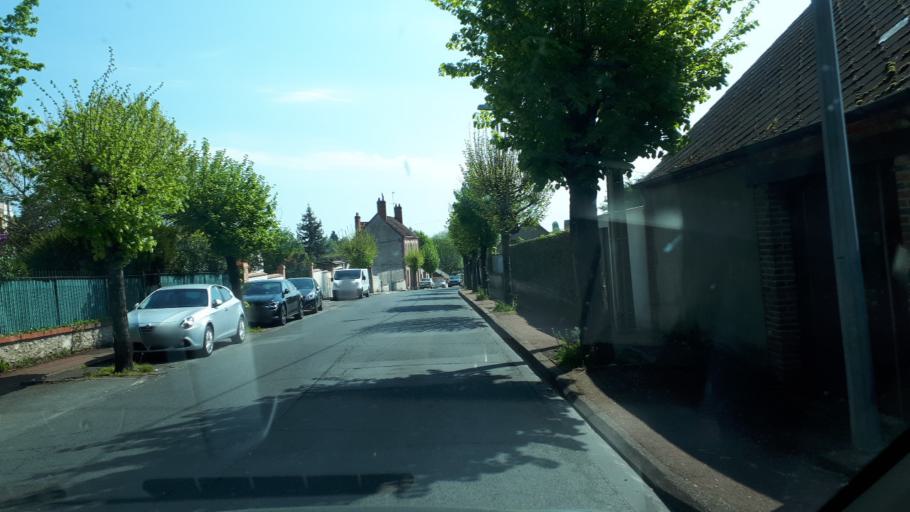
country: FR
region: Centre
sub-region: Departement du Loir-et-Cher
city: Romorantin-Lanthenay
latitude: 47.3611
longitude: 1.7451
